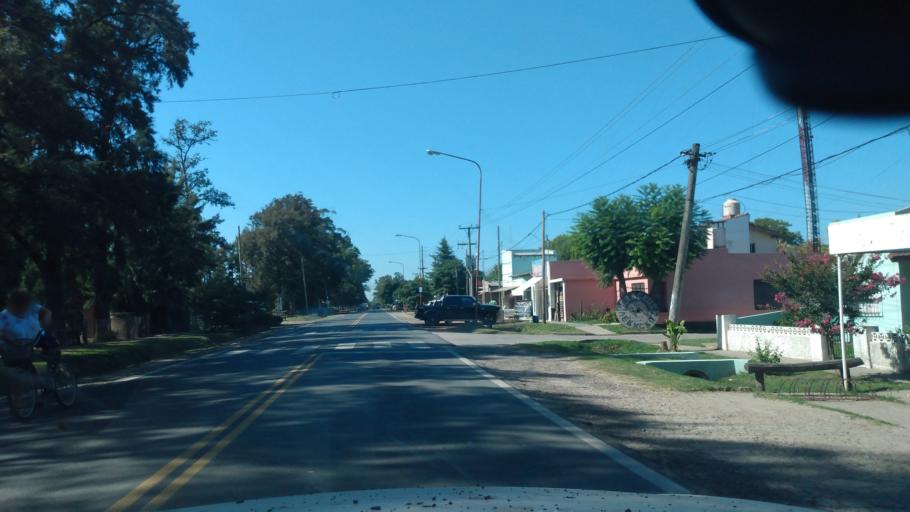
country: AR
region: Buenos Aires
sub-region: Partido de Lujan
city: Lujan
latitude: -34.4974
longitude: -59.0730
